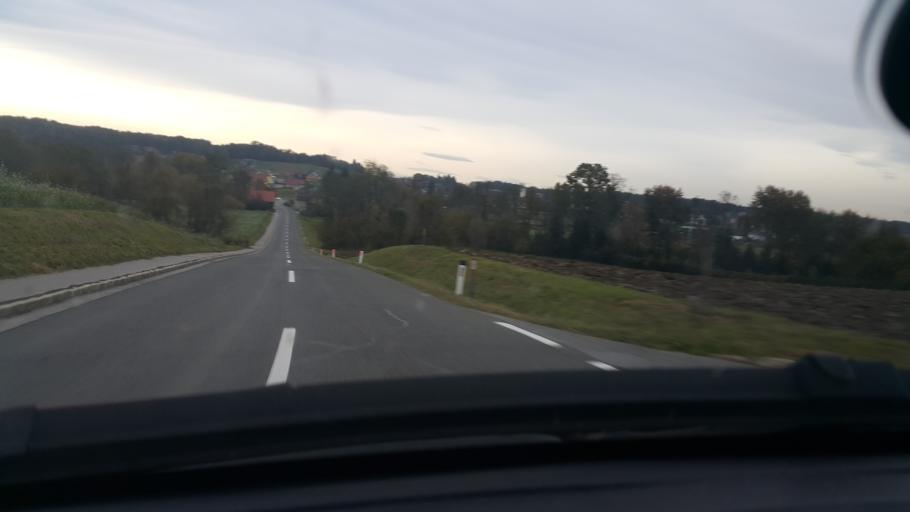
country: AT
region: Styria
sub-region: Politischer Bezirk Deutschlandsberg
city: Wies
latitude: 46.7209
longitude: 15.2959
